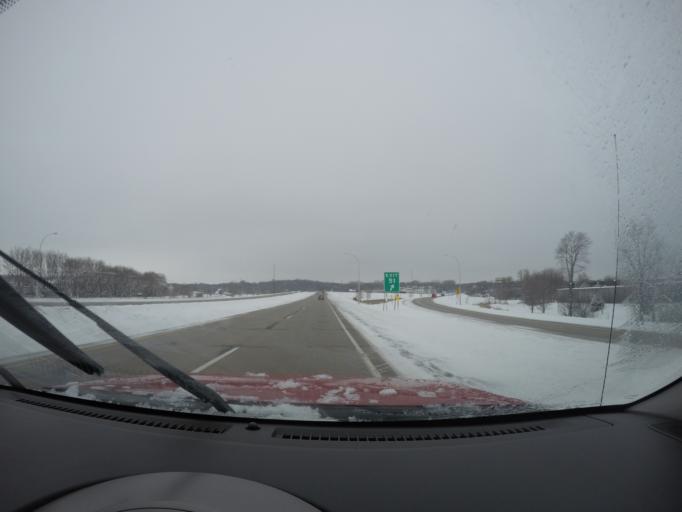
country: US
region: Minnesota
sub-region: Olmsted County
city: Rochester
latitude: 43.9757
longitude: -92.4578
